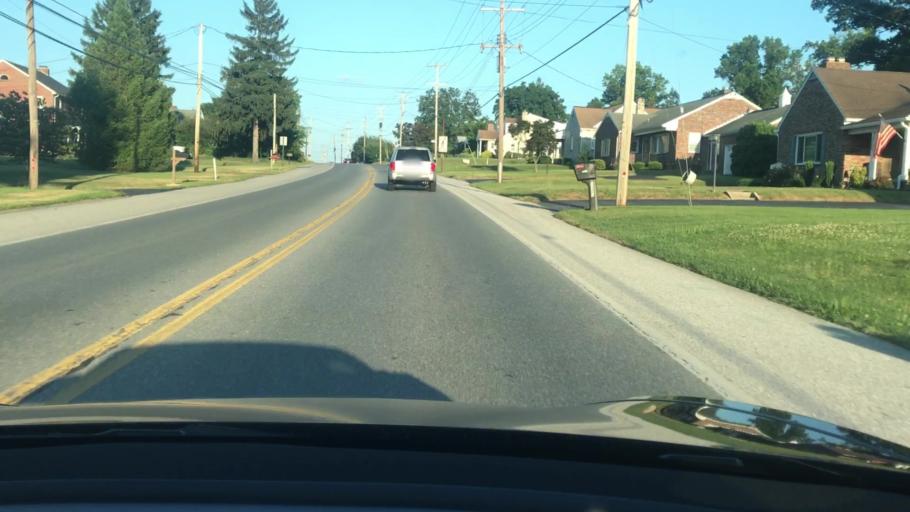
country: US
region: Pennsylvania
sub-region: York County
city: Weigelstown
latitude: 39.9852
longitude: -76.8283
